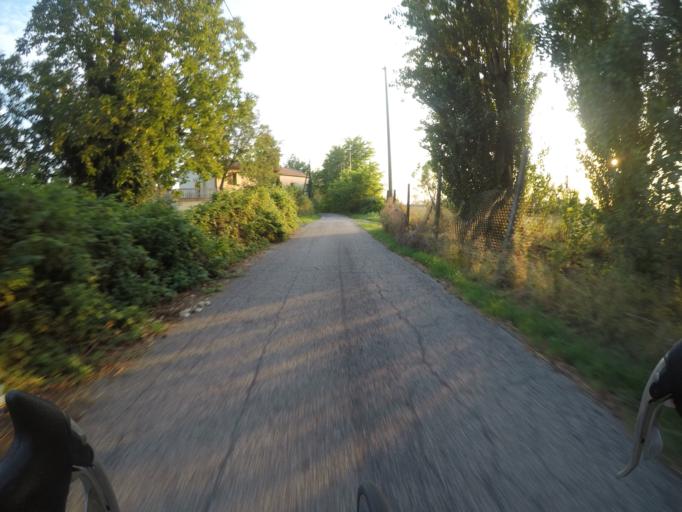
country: IT
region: Veneto
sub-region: Provincia di Rovigo
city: Pincara
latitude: 45.0007
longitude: 11.6033
